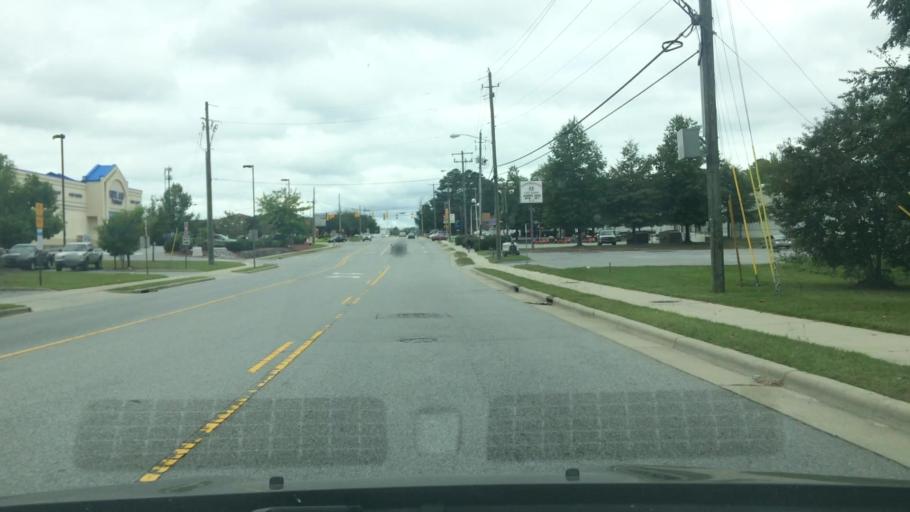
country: US
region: North Carolina
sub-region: Pitt County
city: Greenville
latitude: 35.6007
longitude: -77.3689
